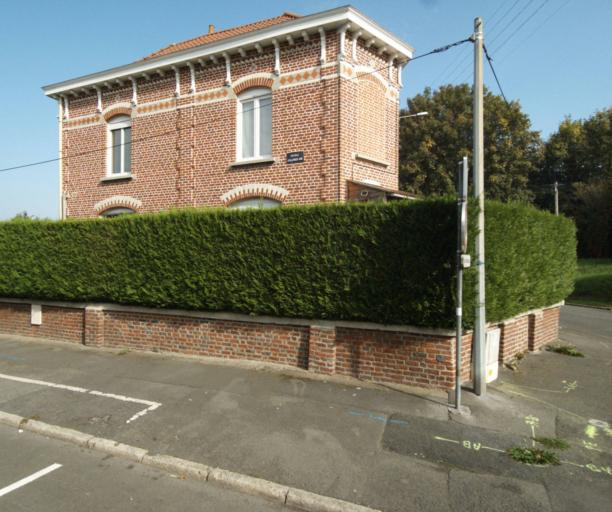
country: FR
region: Nord-Pas-de-Calais
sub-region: Departement du Nord
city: Seclin
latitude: 50.5441
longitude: 3.0316
